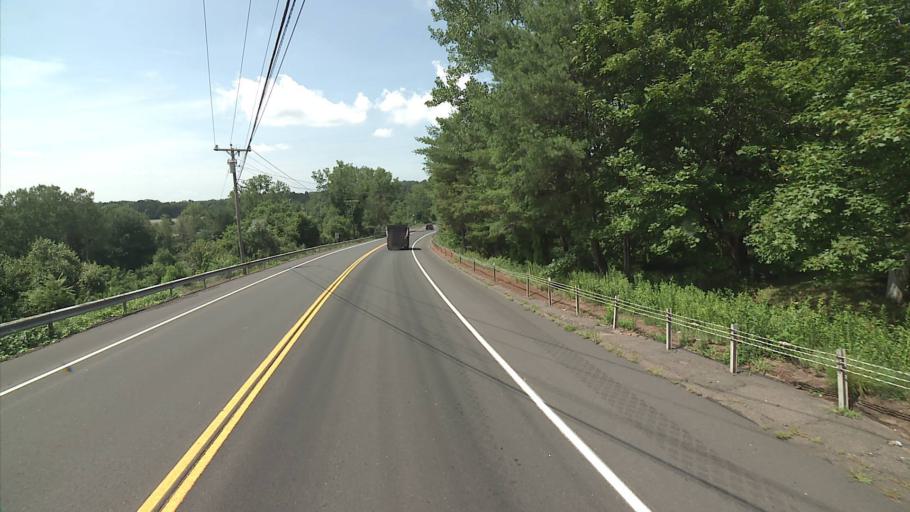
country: US
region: Connecticut
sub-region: Tolland County
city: Rockville
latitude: 41.8520
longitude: -72.4268
